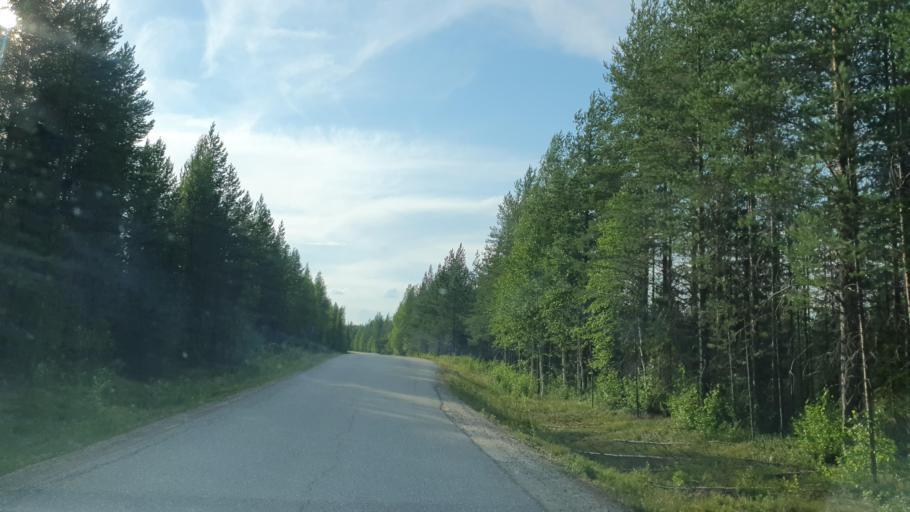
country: FI
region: Kainuu
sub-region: Kehys-Kainuu
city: Kuhmo
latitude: 64.2779
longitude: 29.4298
